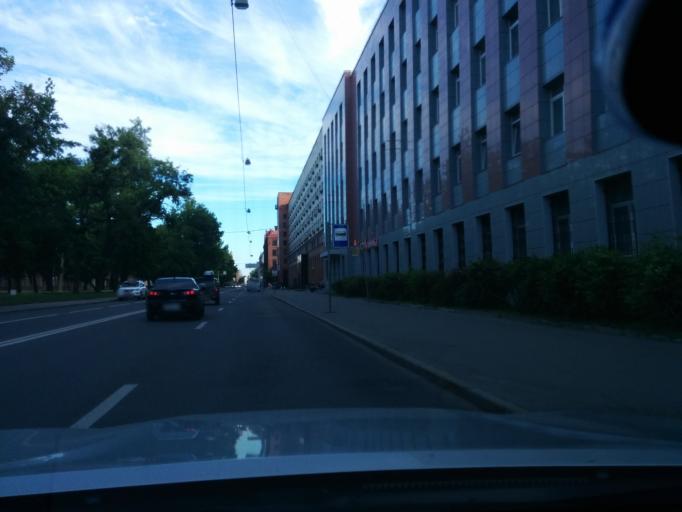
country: RU
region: Leningrad
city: Sampsonievskiy
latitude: 59.9768
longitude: 30.3383
